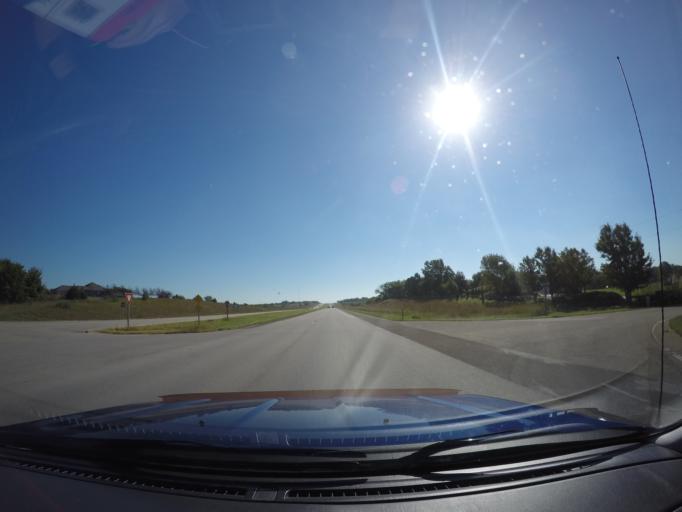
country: US
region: Kansas
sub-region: Pottawatomie County
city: Wamego
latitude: 39.2103
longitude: -96.3635
